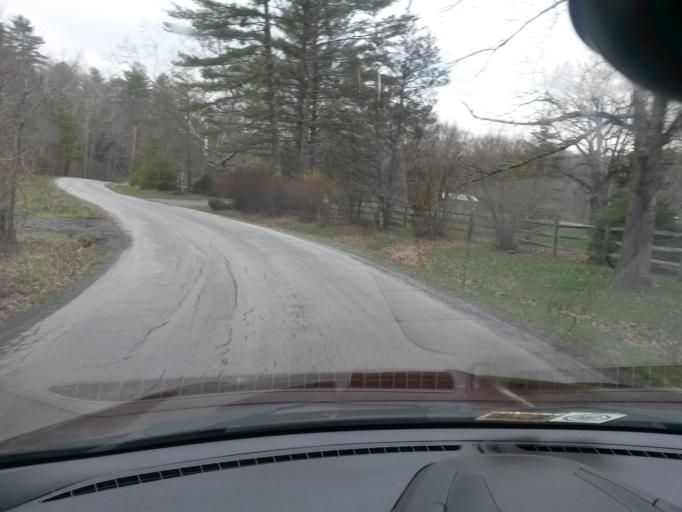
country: US
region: Virginia
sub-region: Bath County
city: Warm Springs
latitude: 38.0541
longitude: -79.8499
